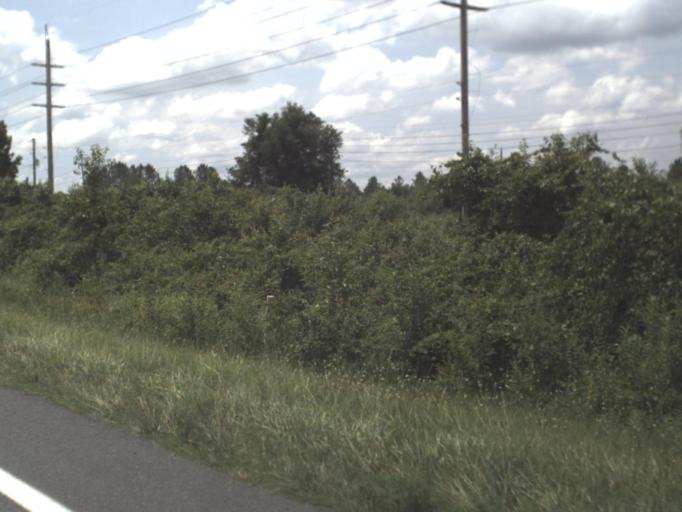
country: US
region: Florida
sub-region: Hamilton County
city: Jasper
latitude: 30.4367
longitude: -82.8725
